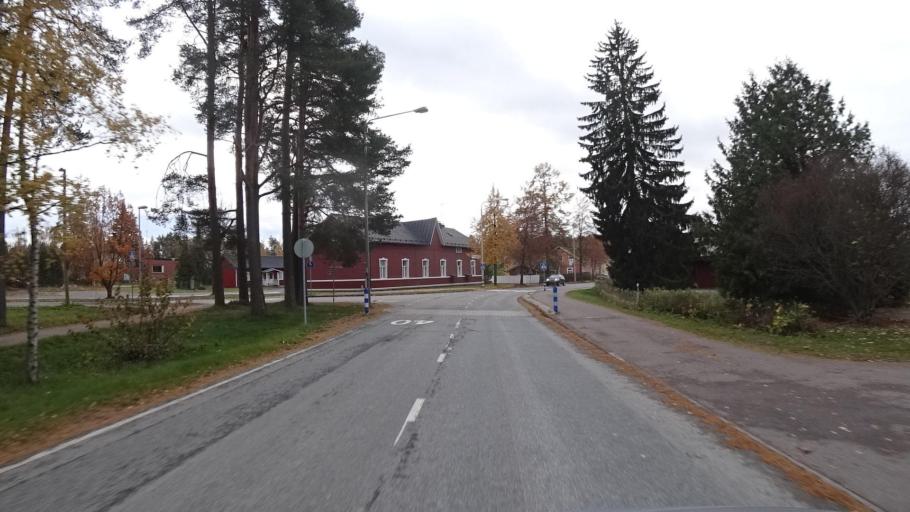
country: FI
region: Central Finland
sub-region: Joutsa
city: Joutsa
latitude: 61.7455
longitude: 26.1204
